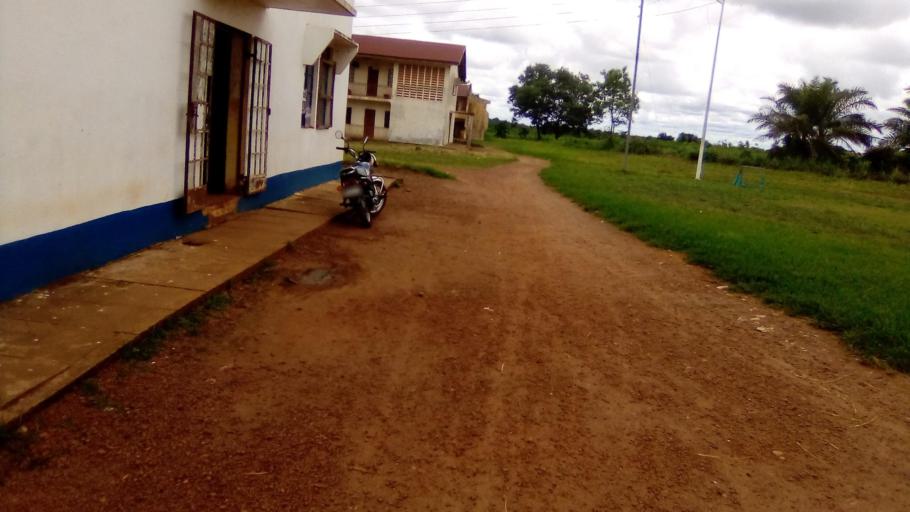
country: SL
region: Southern Province
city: Largo
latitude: 8.1183
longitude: -12.0691
